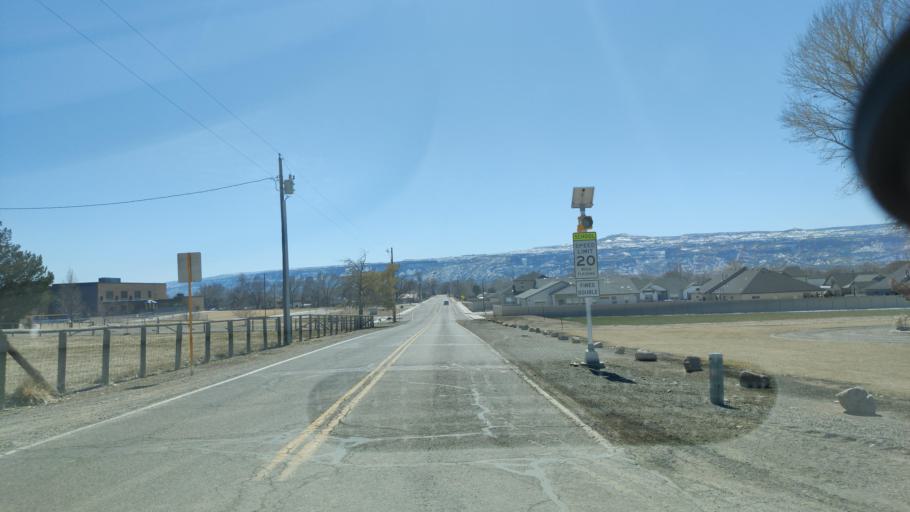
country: US
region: Colorado
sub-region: Mesa County
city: Fruita
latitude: 39.1724
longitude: -108.7105
